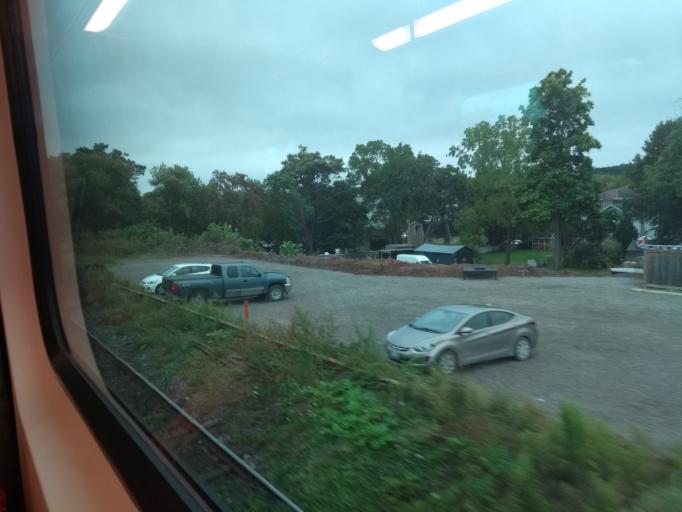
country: CA
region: Ontario
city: Oakville
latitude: 43.1959
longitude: -79.5577
